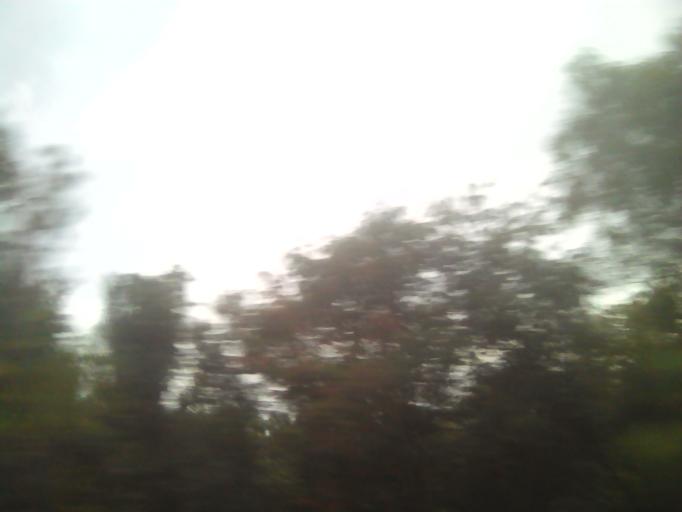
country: MY
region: Penang
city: Butterworth
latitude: 5.4056
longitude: 100.3796
